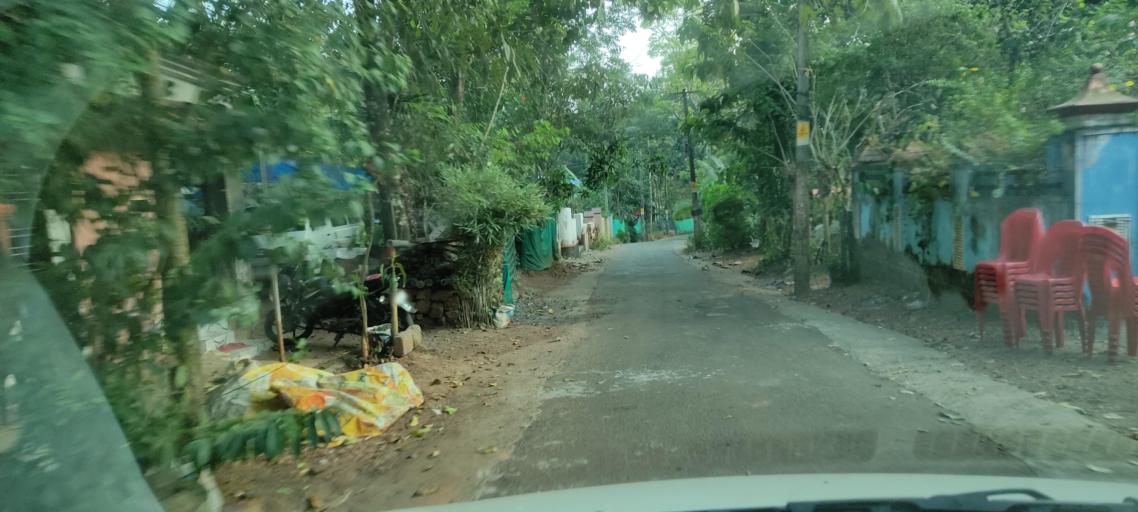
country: IN
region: Kerala
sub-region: Alappuzha
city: Kattanam
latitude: 9.1659
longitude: 76.5902
